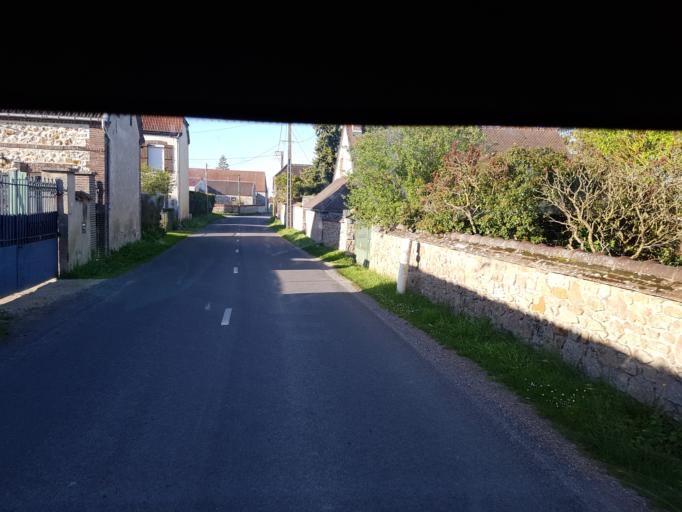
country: FR
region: Champagne-Ardenne
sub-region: Departement de l'Aube
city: Marigny-le-Chatel
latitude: 48.3868
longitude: 3.6533
